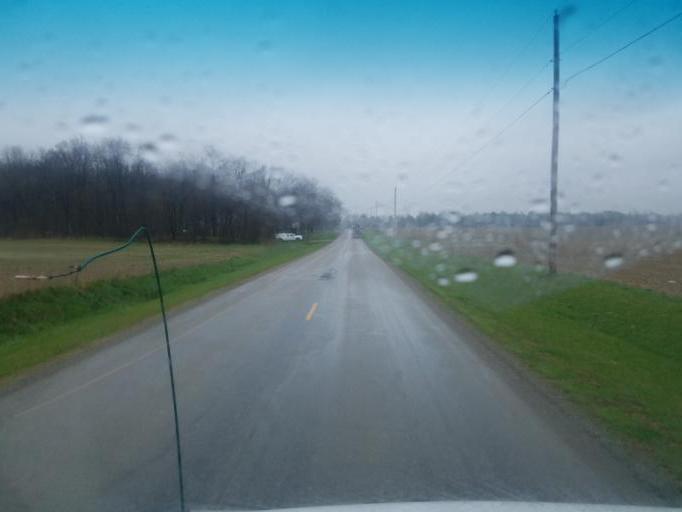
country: US
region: Ohio
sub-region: Wyandot County
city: Carey
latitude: 40.9855
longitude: -83.2726
